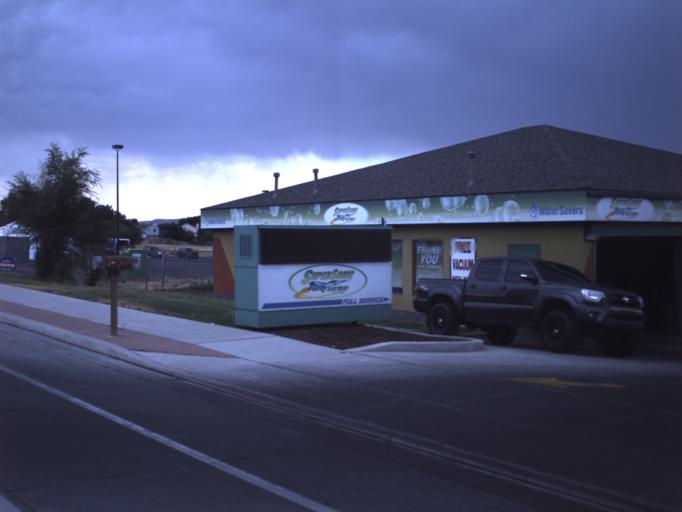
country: US
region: Utah
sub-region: Salt Lake County
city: White City
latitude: 40.5583
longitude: -111.8723
